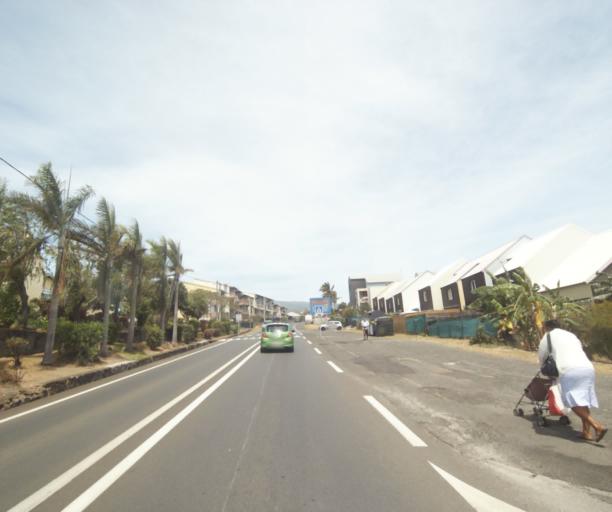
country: RE
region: Reunion
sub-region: Reunion
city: Saint-Paul
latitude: -21.0426
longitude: 55.2562
